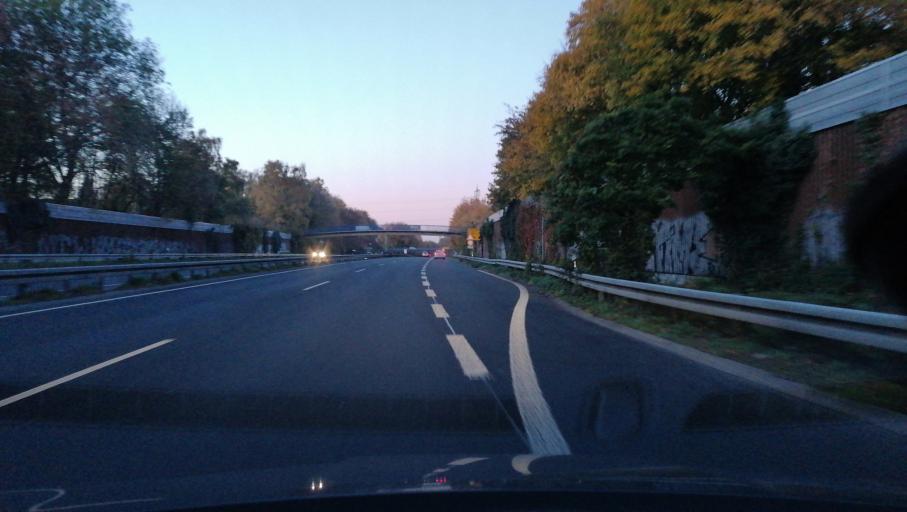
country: DE
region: North Rhine-Westphalia
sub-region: Regierungsbezirk Arnsberg
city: Dortmund
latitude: 51.4665
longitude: 7.4820
